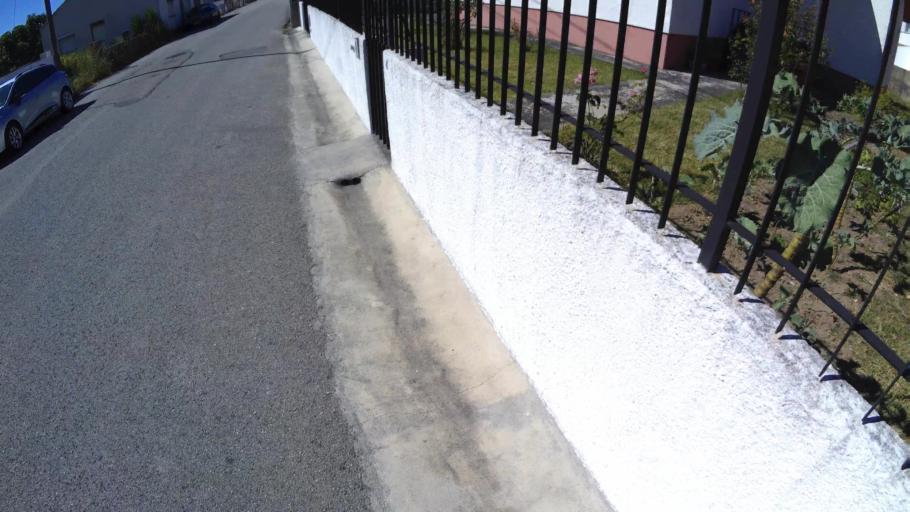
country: PT
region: Aveiro
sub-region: Aveiro
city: Aveiro
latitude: 40.6609
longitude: -8.6221
